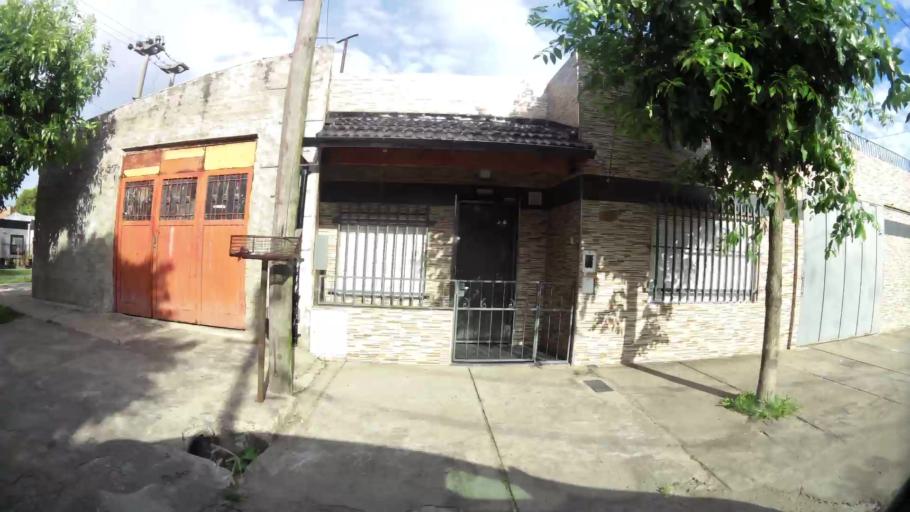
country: AR
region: Santa Fe
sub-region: Departamento de Rosario
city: Rosario
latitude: -32.9809
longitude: -60.6775
